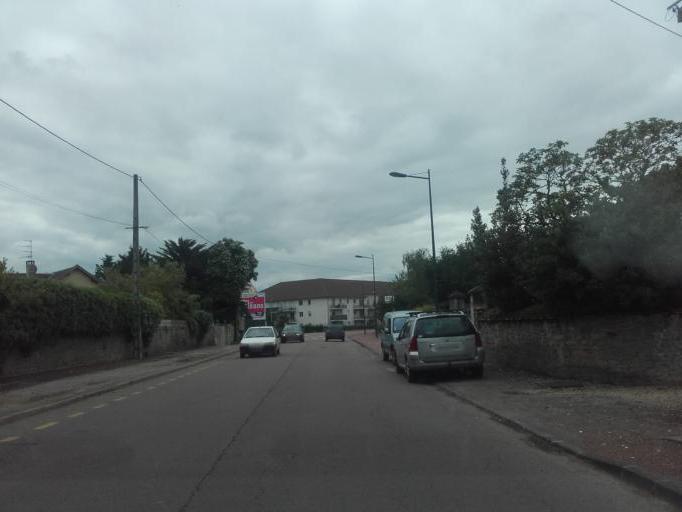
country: FR
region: Bourgogne
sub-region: Departement de la Cote-d'Or
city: Beaune
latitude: 47.0182
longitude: 4.8451
